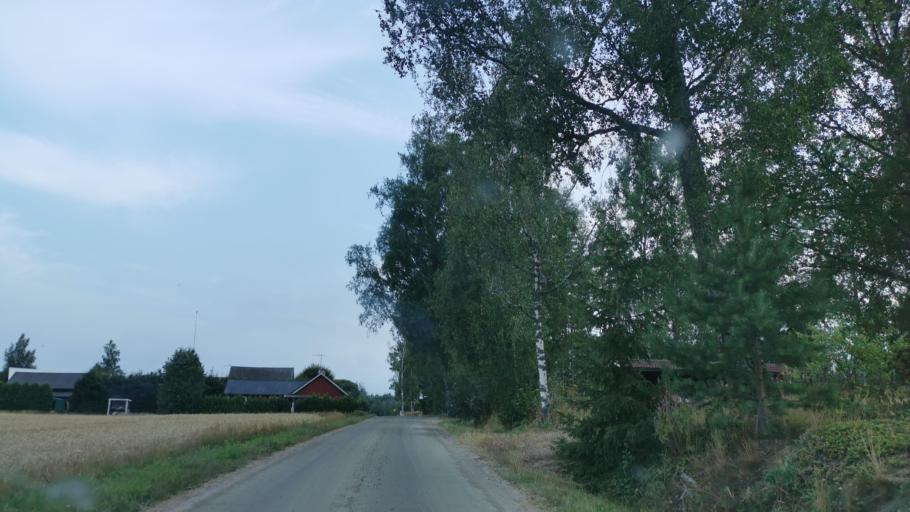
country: SE
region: OEstergoetland
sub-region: Norrkopings Kommun
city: Svartinge
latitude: 58.7209
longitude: 15.9500
